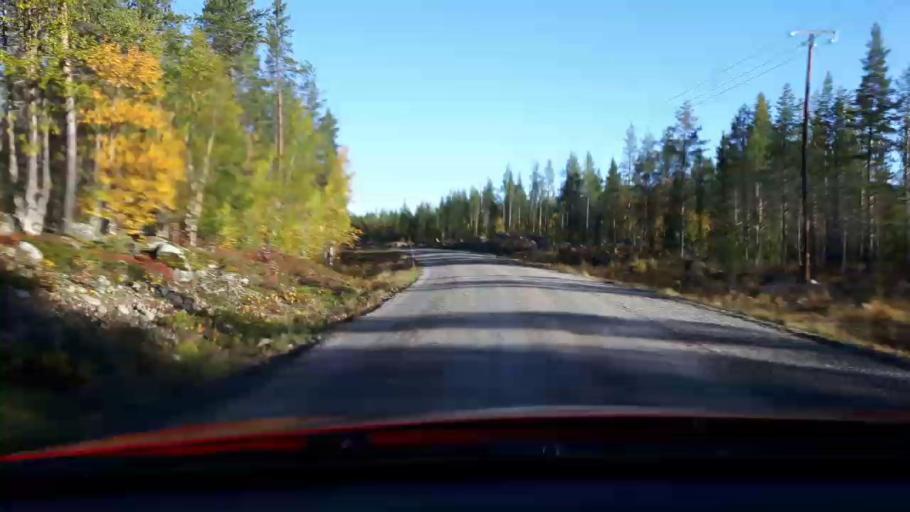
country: SE
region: Jaemtland
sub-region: Stroemsunds Kommun
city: Stroemsund
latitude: 64.3860
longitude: 15.1518
